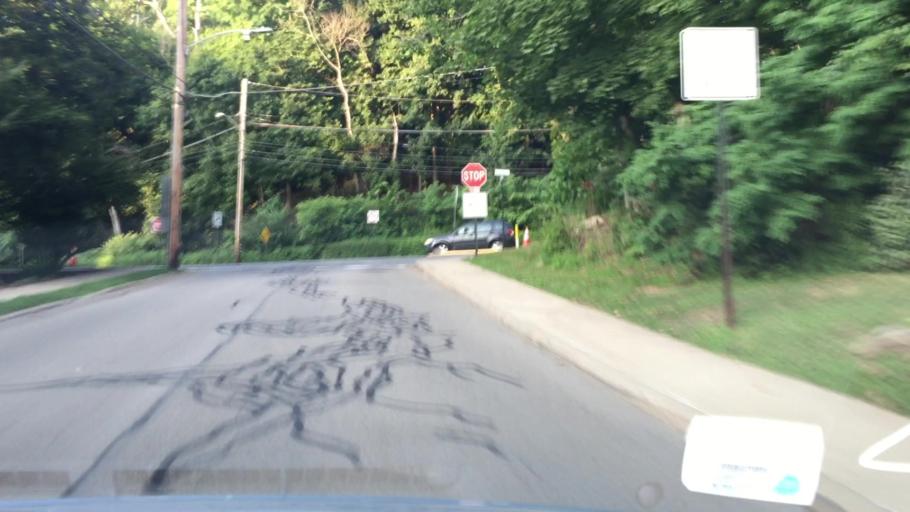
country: US
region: Pennsylvania
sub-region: Allegheny County
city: Edgeworth
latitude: 40.5461
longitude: -80.1896
